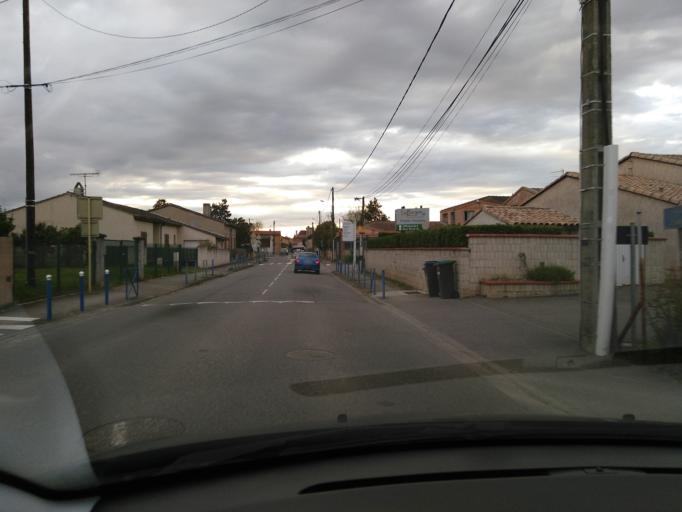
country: FR
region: Midi-Pyrenees
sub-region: Departement de la Haute-Garonne
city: La Salvetat-Saint-Gilles
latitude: 43.5762
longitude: 1.2762
